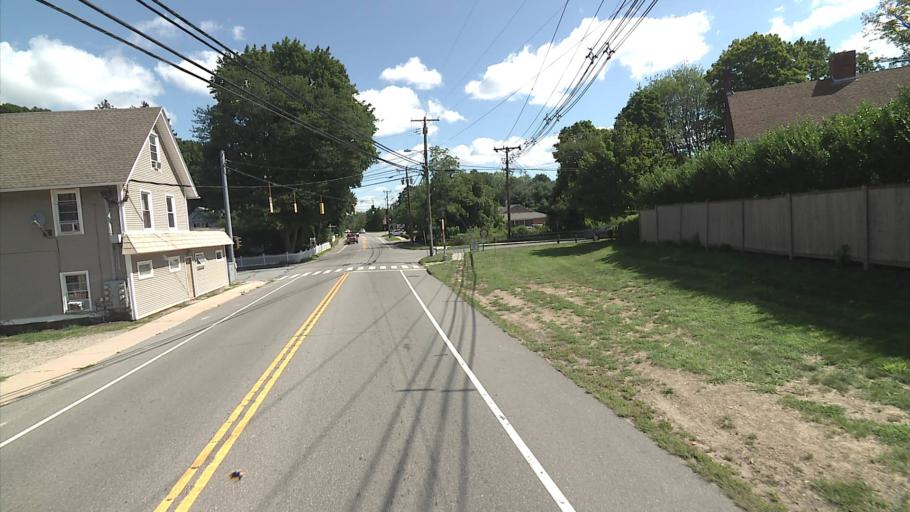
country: US
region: Connecticut
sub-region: Middlesex County
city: Westbrook Center
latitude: 41.2825
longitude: -72.4560
